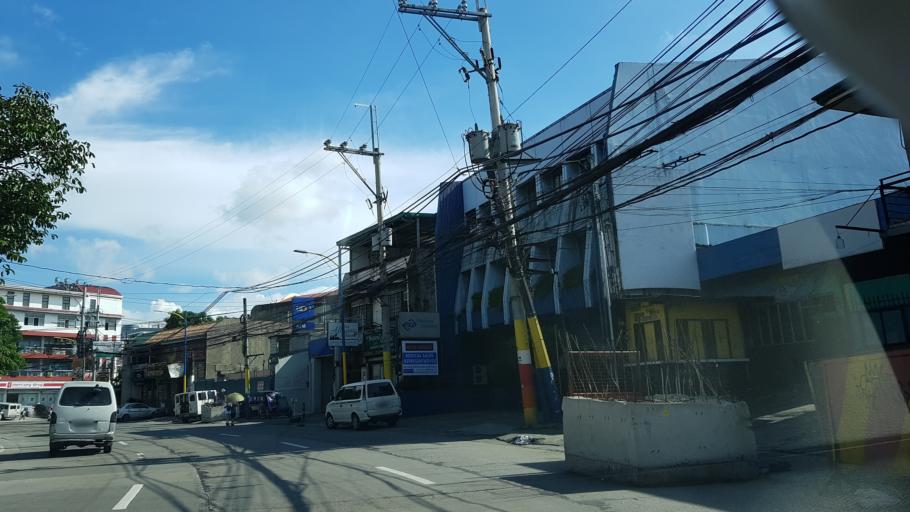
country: PH
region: Metro Manila
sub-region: Mandaluyong
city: Mandaluyong City
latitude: 14.5777
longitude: 121.0328
